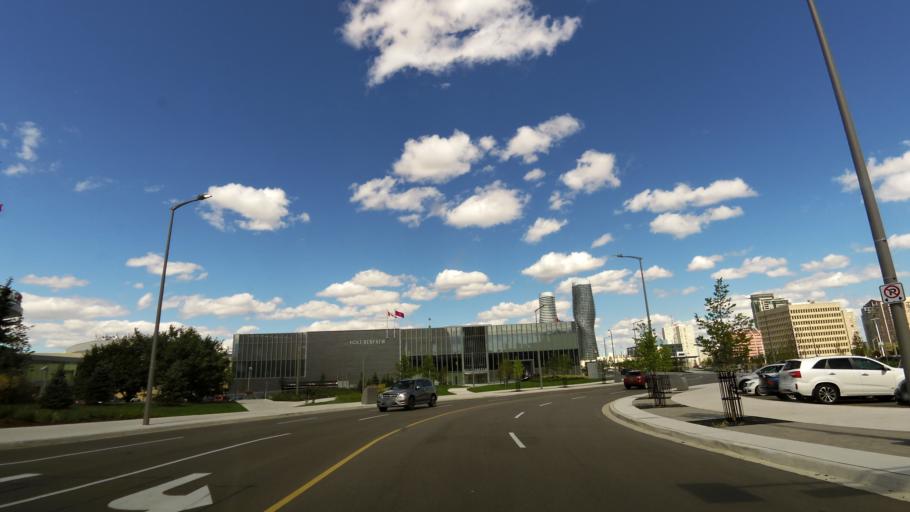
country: CA
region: Ontario
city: Mississauga
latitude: 43.5899
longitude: -79.6442
